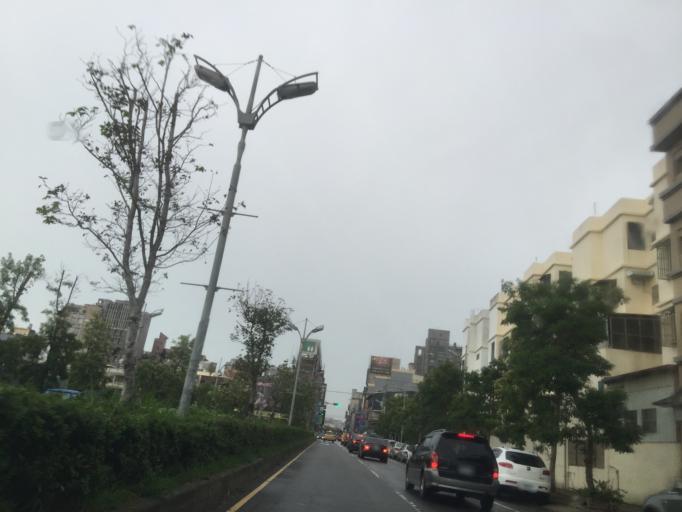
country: TW
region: Taiwan
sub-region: Hsinchu
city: Zhubei
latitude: 24.8234
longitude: 121.0076
